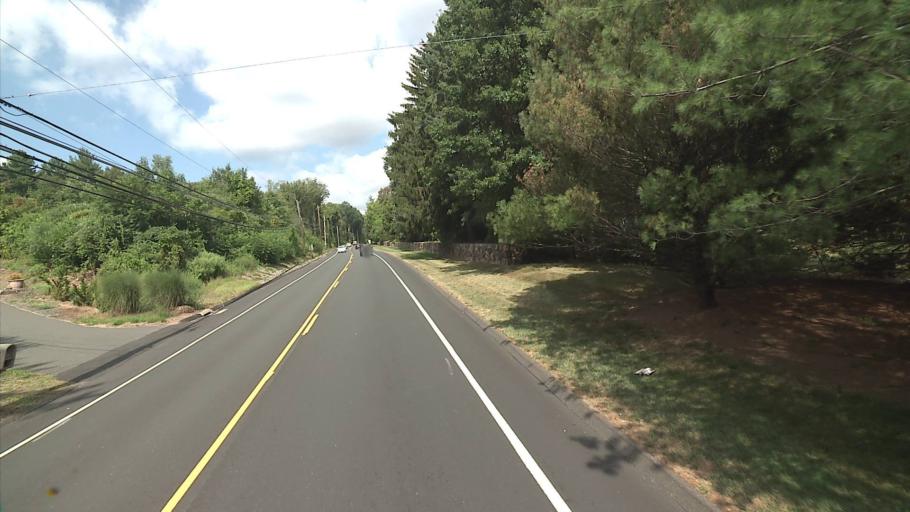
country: US
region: Connecticut
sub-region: Hartford County
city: Weatogue
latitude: 41.8328
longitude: -72.7759
